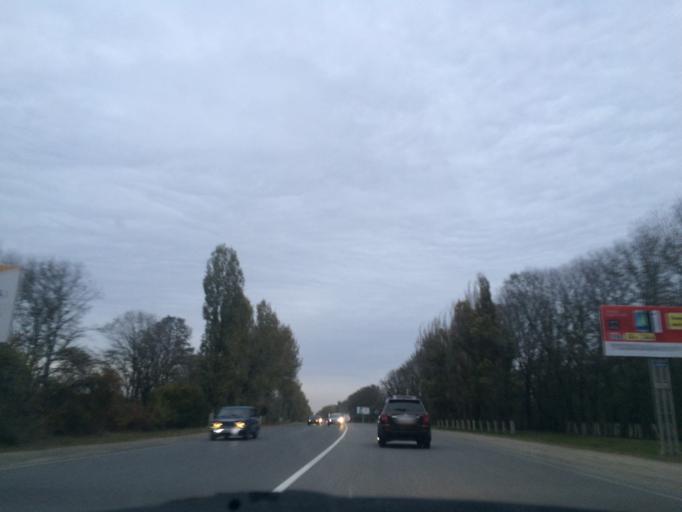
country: RU
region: Rostov
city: Novocherkassk
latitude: 47.4192
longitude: 40.0215
